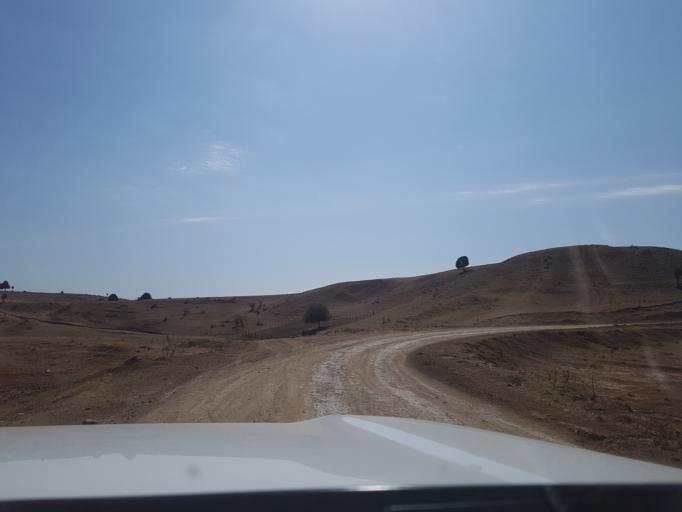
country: TM
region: Ahal
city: Baharly
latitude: 38.3245
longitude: 56.9538
